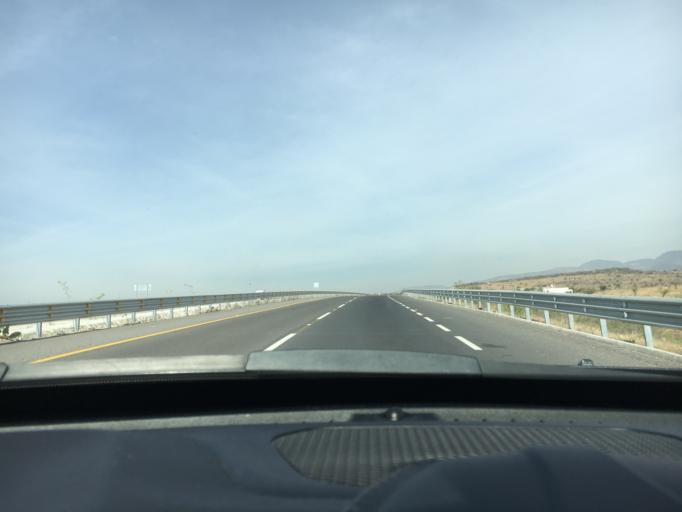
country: MX
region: Guanajuato
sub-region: Silao de la Victoria
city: El Refugio de los Sauces
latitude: 21.0491
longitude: -101.5274
